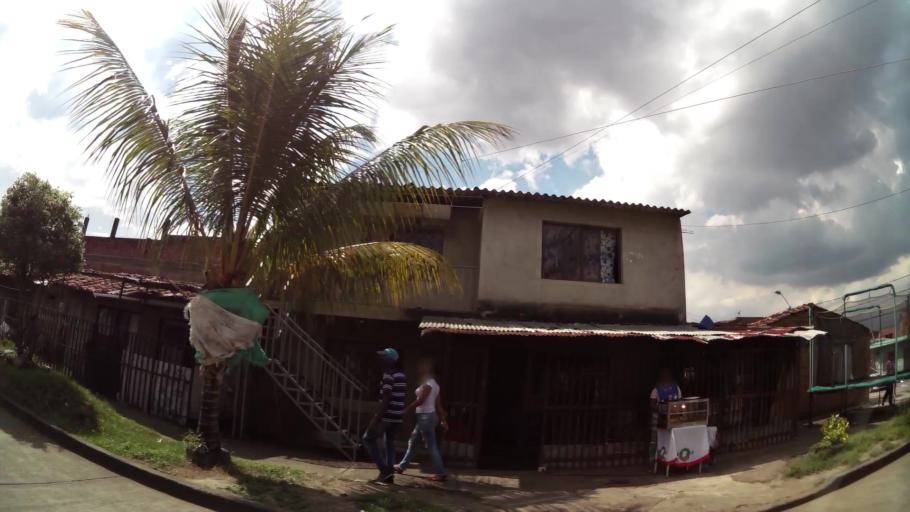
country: CO
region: Valle del Cauca
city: Cali
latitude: 3.4005
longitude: -76.5135
